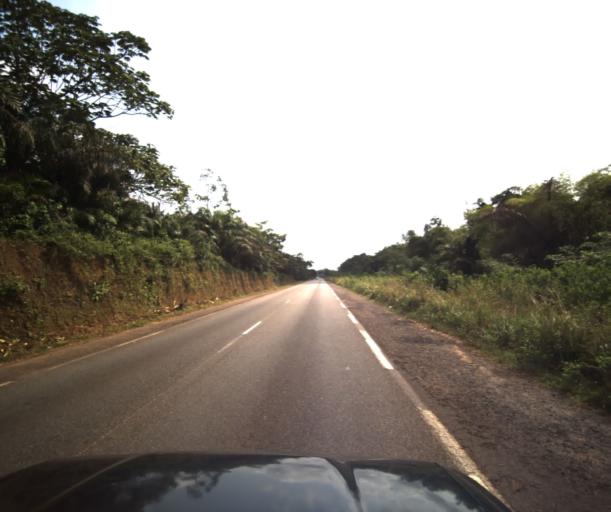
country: CM
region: Littoral
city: Edea
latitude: 3.7672
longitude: 10.1833
